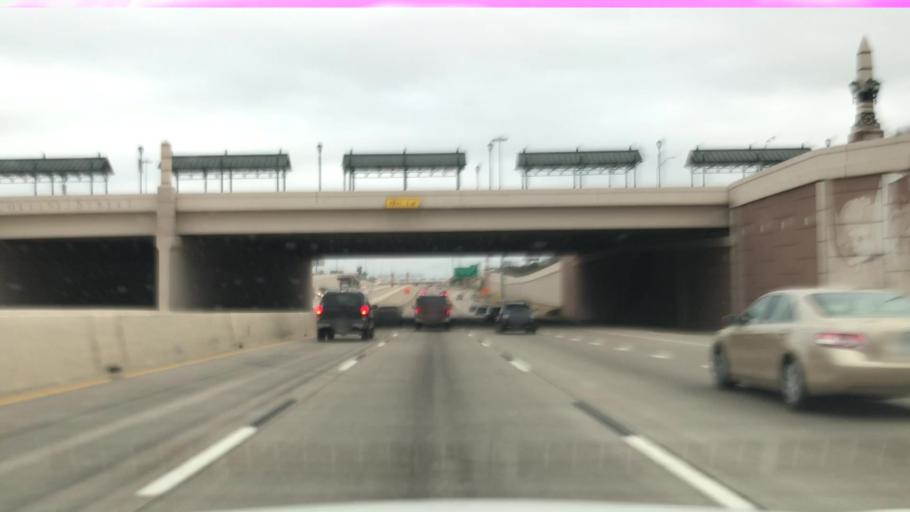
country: US
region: Texas
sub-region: Tarrant County
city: Arlington
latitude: 32.7595
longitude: -97.0982
